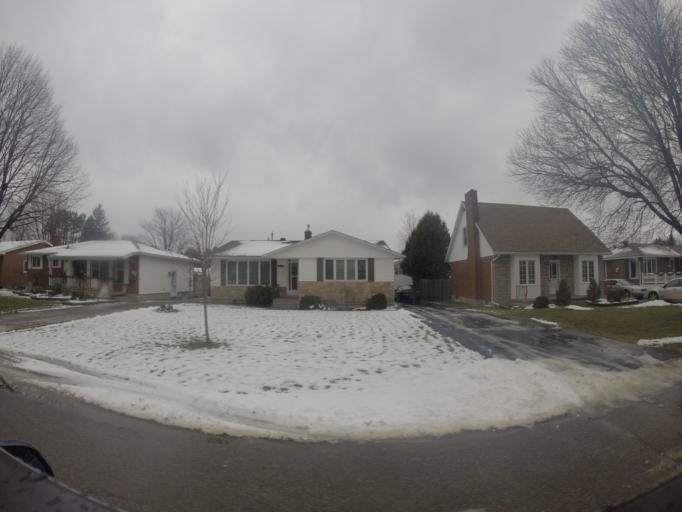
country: CA
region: Ontario
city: Greater Sudbury
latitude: 46.5240
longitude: -80.9356
